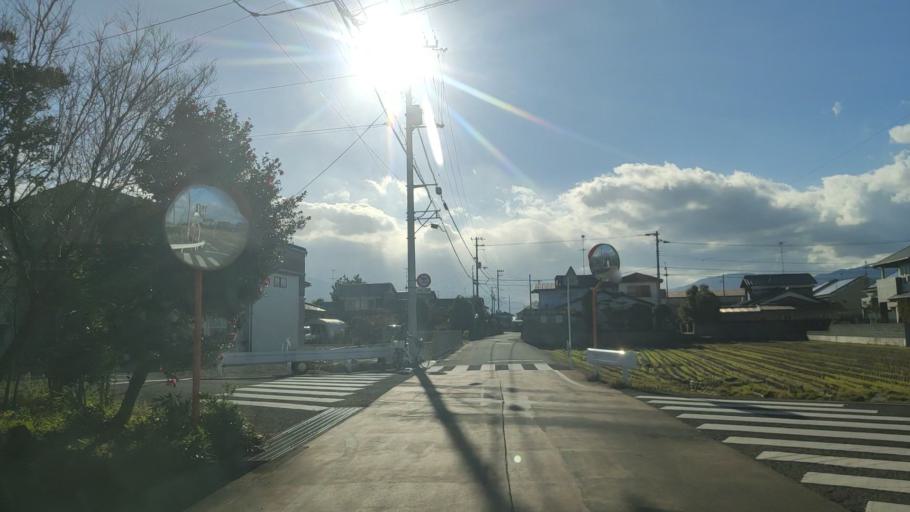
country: JP
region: Ehime
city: Saijo
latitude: 33.9110
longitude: 133.0973
